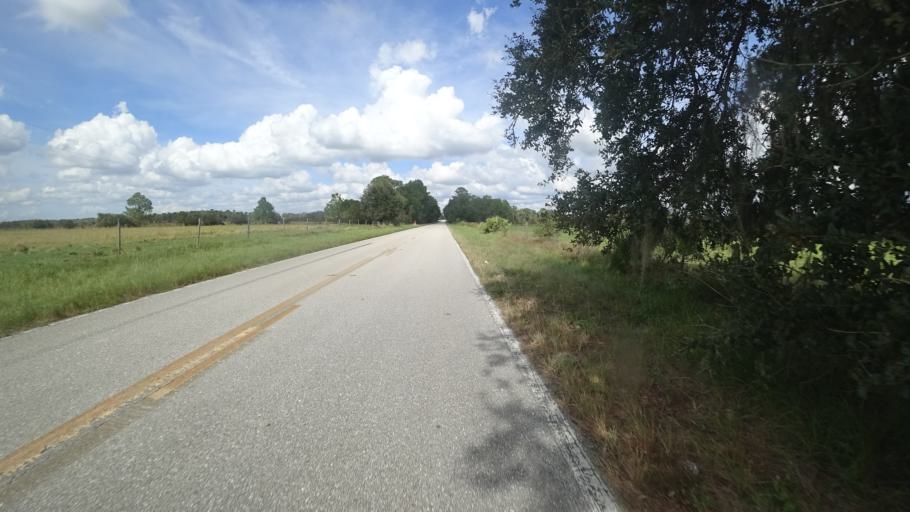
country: US
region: Florida
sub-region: Hillsborough County
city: Wimauma
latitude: 27.6412
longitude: -82.2286
